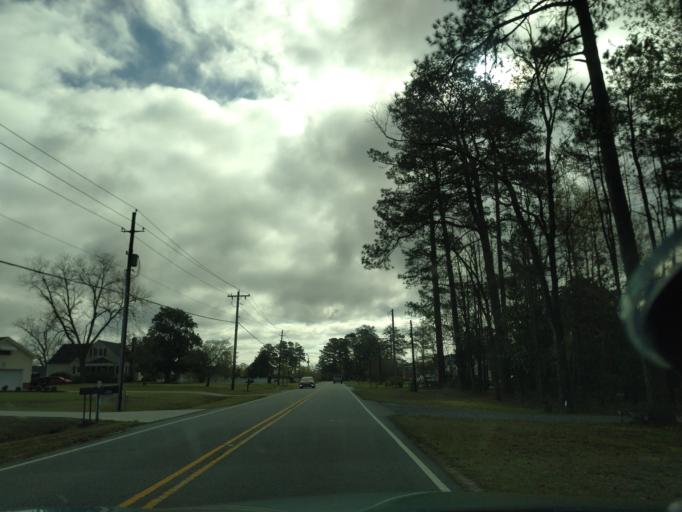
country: US
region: North Carolina
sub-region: Chowan County
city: Edenton
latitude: 36.0572
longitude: -76.6580
